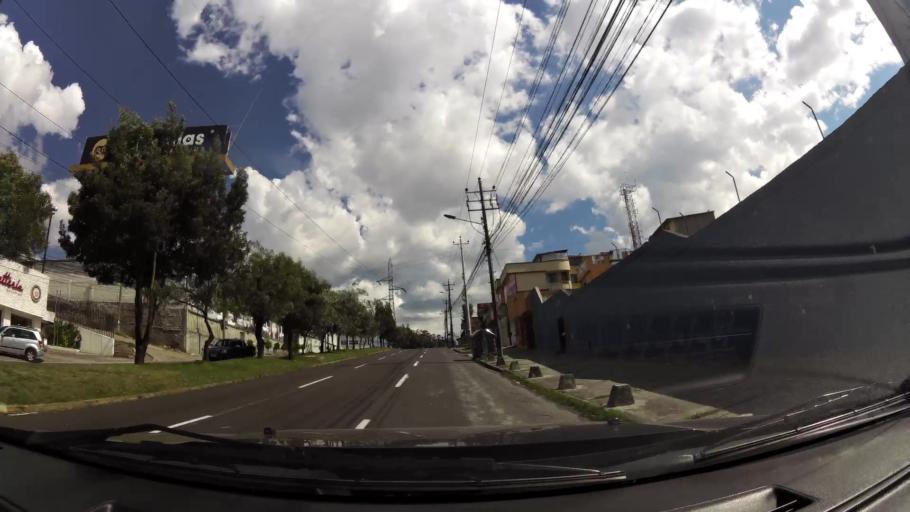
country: EC
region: Pichincha
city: Quito
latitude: -0.1066
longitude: -78.4729
